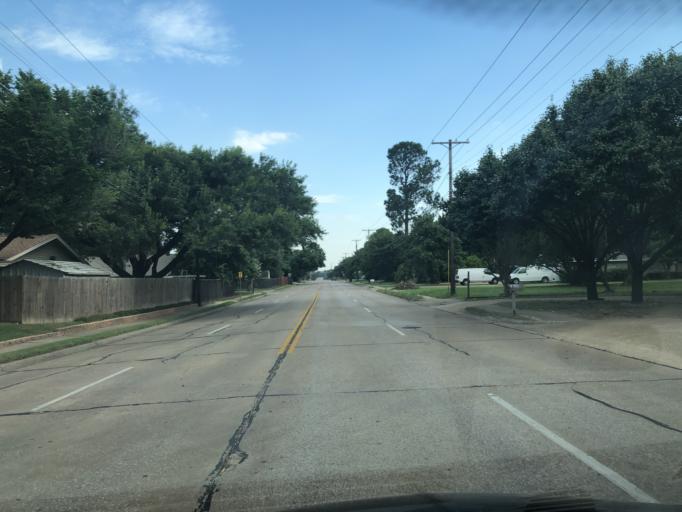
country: US
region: Texas
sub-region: Dallas County
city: Irving
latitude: 32.7982
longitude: -96.9771
